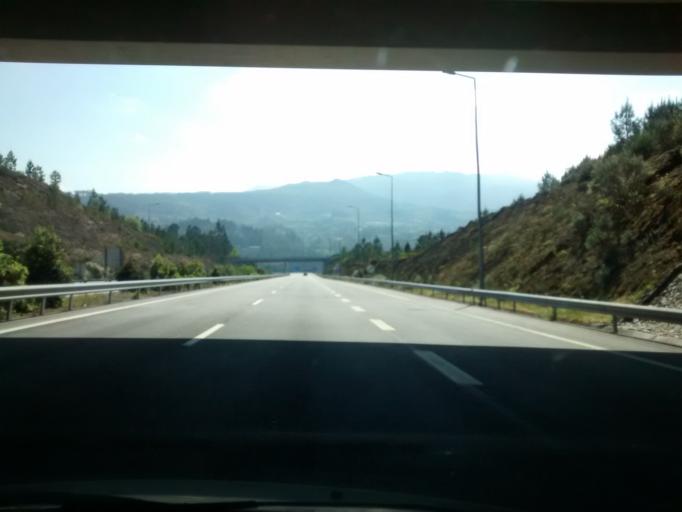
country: PT
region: Braga
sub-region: Cabeceiras de Basto
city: Cabeceiras de Basto
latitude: 41.4733
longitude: -7.9473
